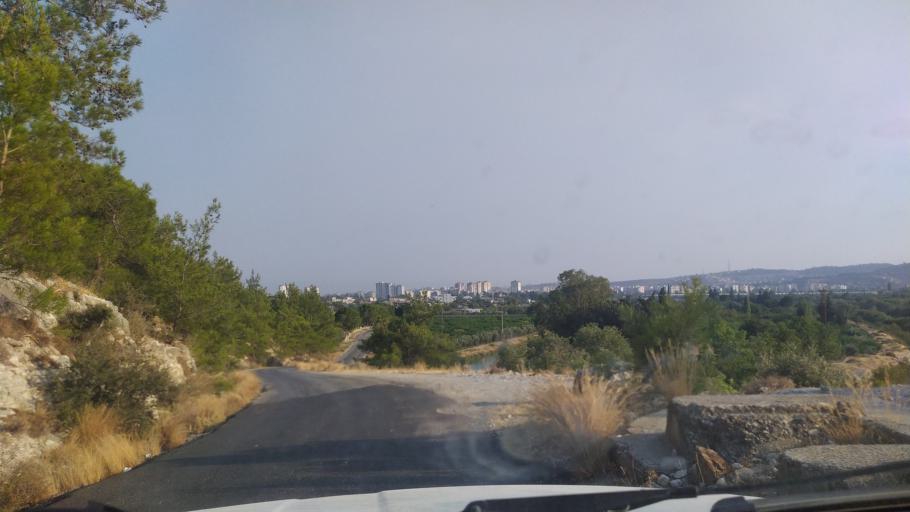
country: TR
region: Mersin
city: Silifke
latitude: 36.4028
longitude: 33.9250
